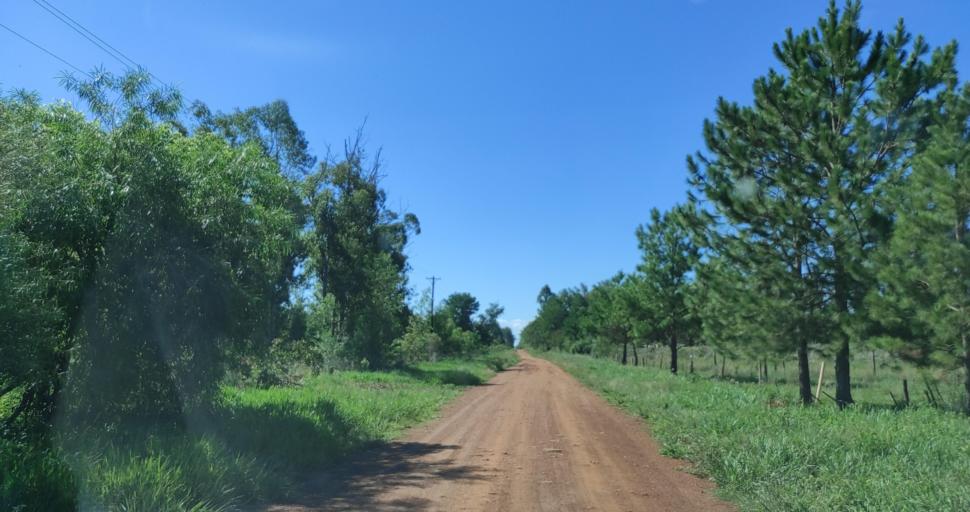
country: AR
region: Misiones
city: Garupa
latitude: -27.4727
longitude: -55.7984
